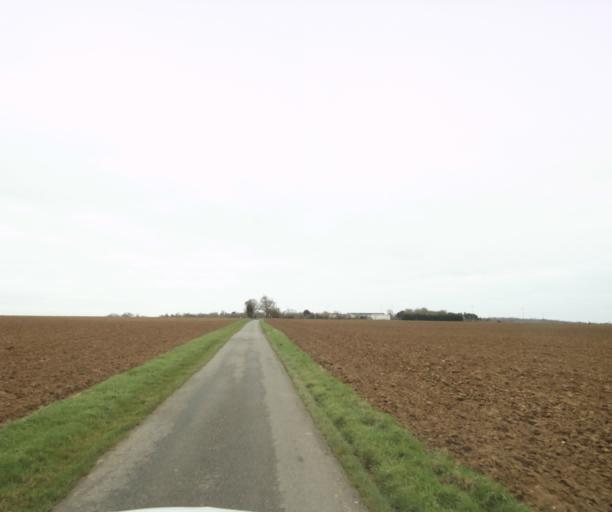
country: FR
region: Poitou-Charentes
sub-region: Departement de la Charente-Maritime
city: Nieul-sur-Mer
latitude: 46.1947
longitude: -1.1660
